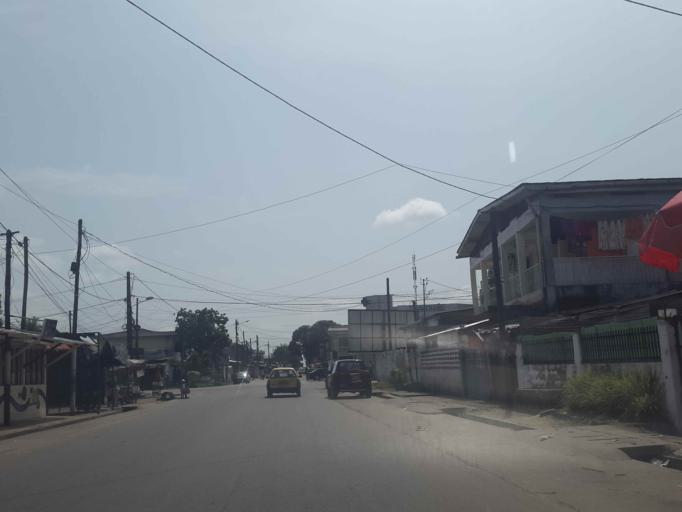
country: CM
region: Littoral
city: Douala
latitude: 4.0674
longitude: 9.7121
